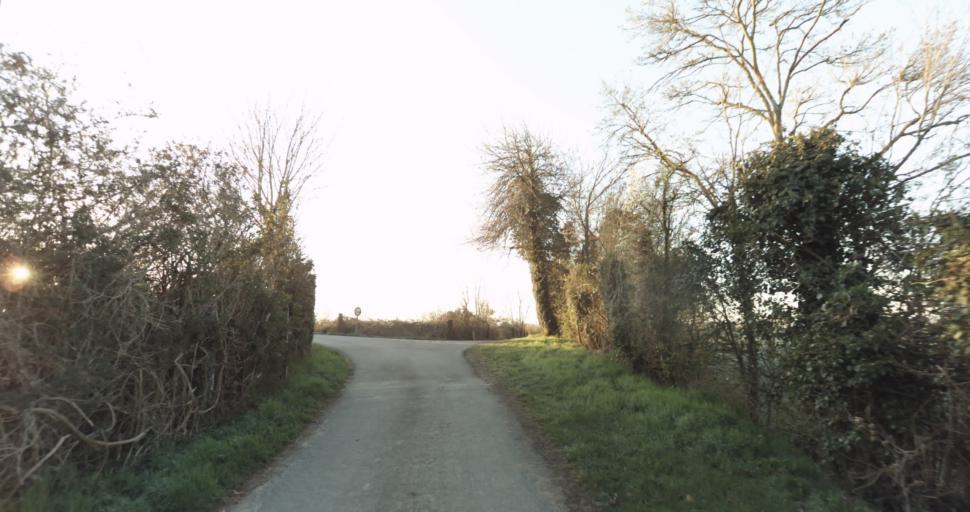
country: FR
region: Lower Normandy
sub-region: Departement du Calvados
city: Saint-Pierre-sur-Dives
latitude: 49.0374
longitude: -0.0363
